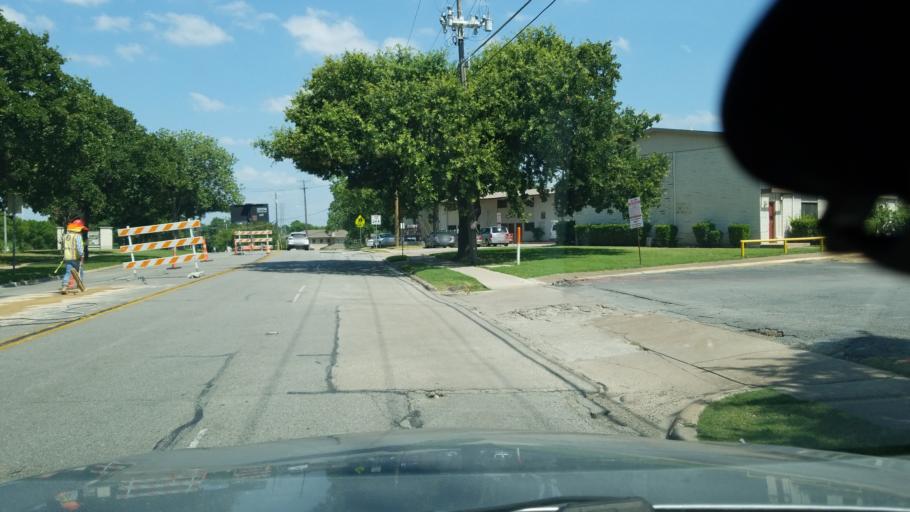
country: US
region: Texas
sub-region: Dallas County
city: Irving
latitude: 32.8192
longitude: -96.9554
